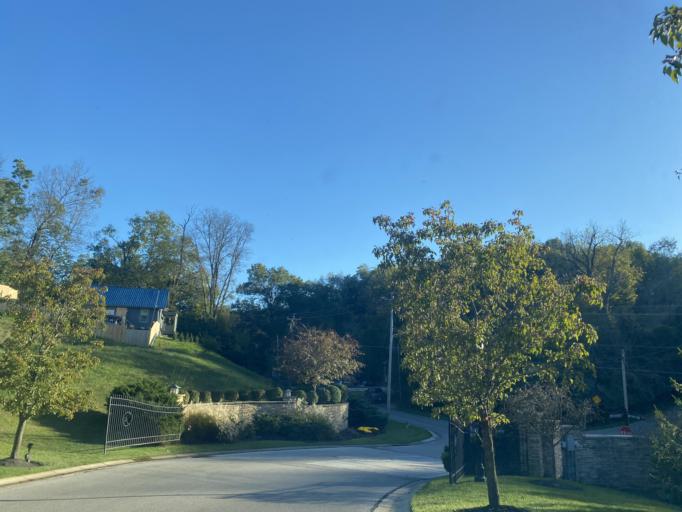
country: US
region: Kentucky
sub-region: Campbell County
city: Dayton
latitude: 39.1088
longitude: -84.4649
